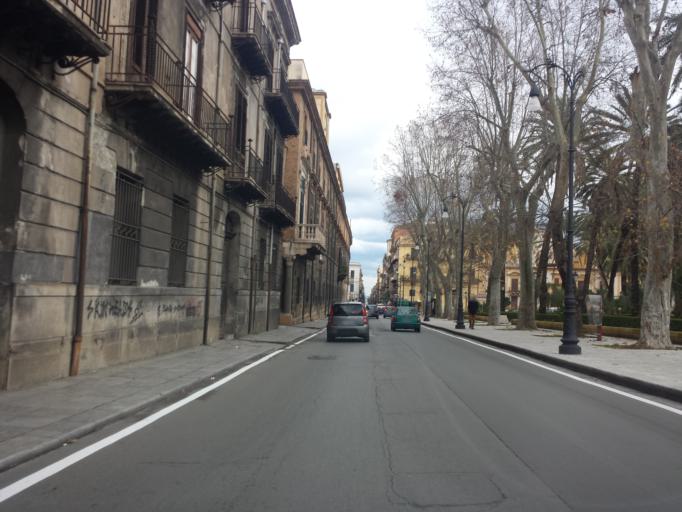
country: IT
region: Sicily
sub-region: Palermo
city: Palermo
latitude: 38.1128
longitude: 13.3543
